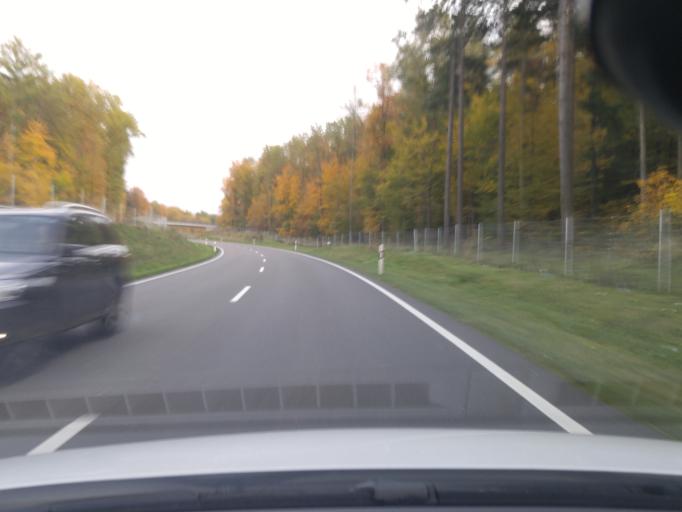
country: DE
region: Baden-Wuerttemberg
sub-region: Karlsruhe Region
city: Muhlhausen
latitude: 49.2441
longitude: 8.7119
